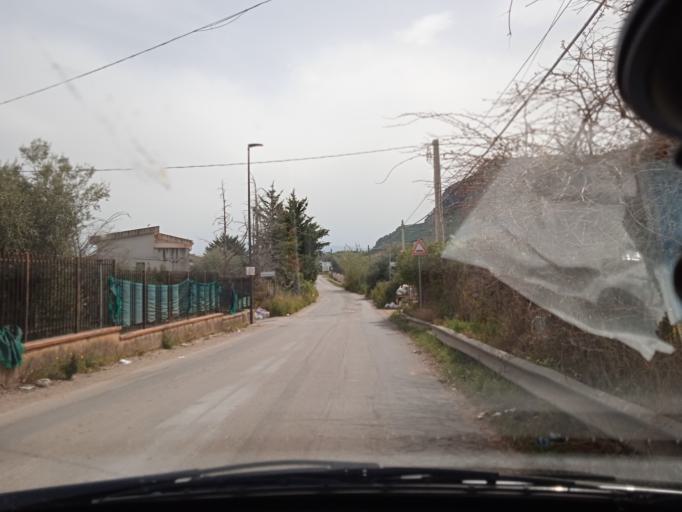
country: IT
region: Sicily
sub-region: Palermo
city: Torre Colonna-Sperone
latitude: 38.0289
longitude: 13.5713
